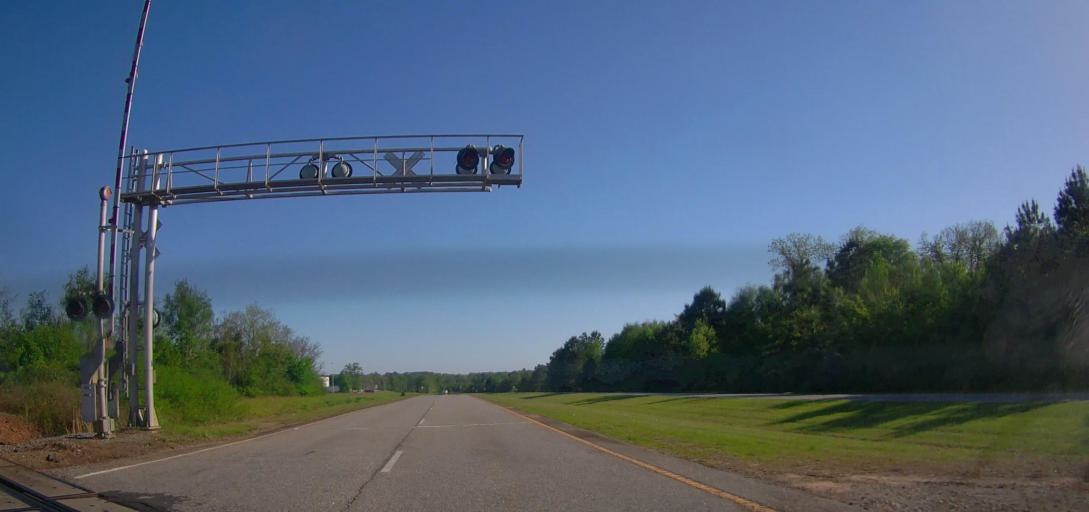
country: US
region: Georgia
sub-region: Houston County
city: Perry
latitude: 32.4648
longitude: -83.7778
